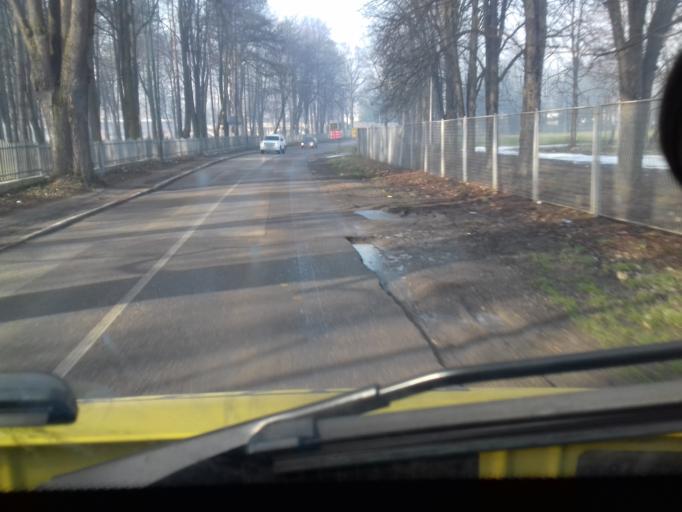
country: BA
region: Federation of Bosnia and Herzegovina
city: Visoko
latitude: 43.9893
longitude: 18.1859
